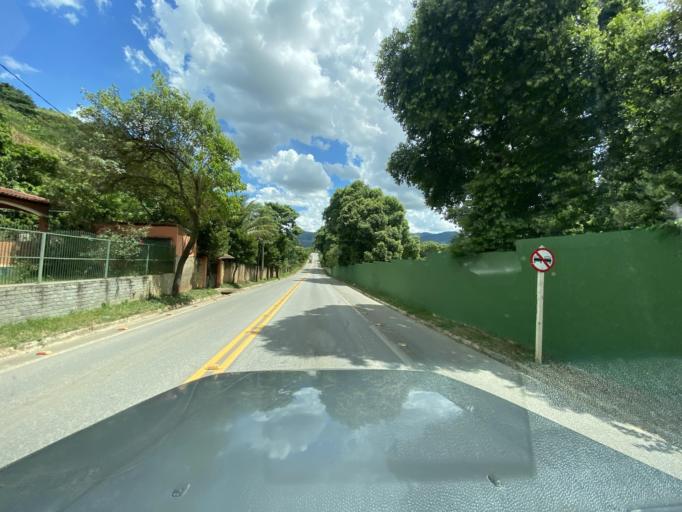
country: BR
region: Espirito Santo
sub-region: Jeronimo Monteiro
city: Jeronimo Monteiro
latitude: -20.7911
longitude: -41.3941
